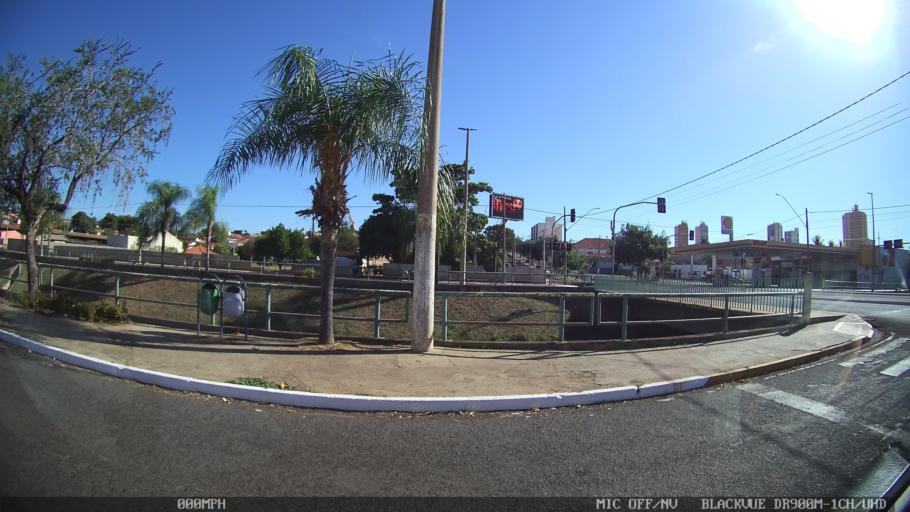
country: BR
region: Sao Paulo
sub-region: Olimpia
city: Olimpia
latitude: -20.7408
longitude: -48.9099
